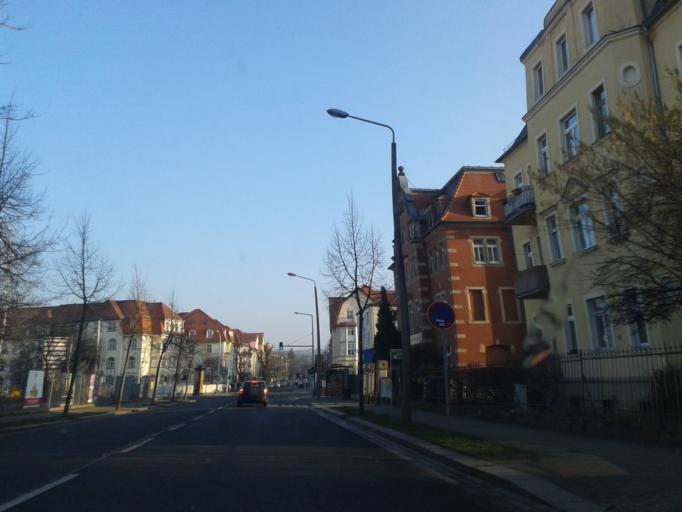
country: DE
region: Saxony
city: Albertstadt
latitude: 51.0420
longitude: 13.7947
